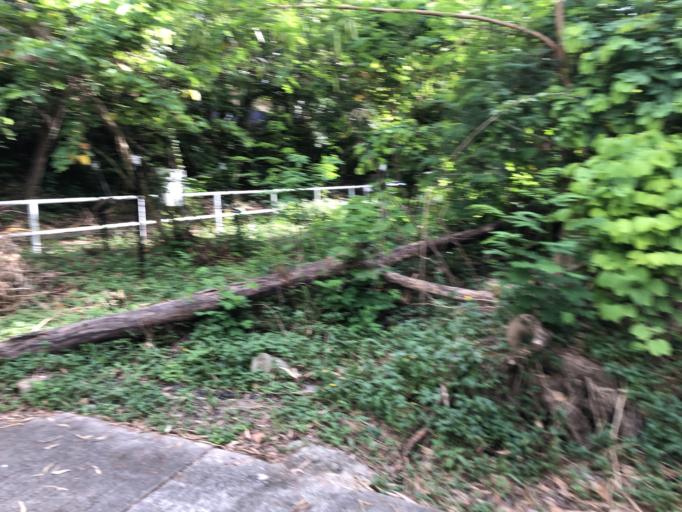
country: HK
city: Tai O
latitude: 22.2794
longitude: 113.9338
